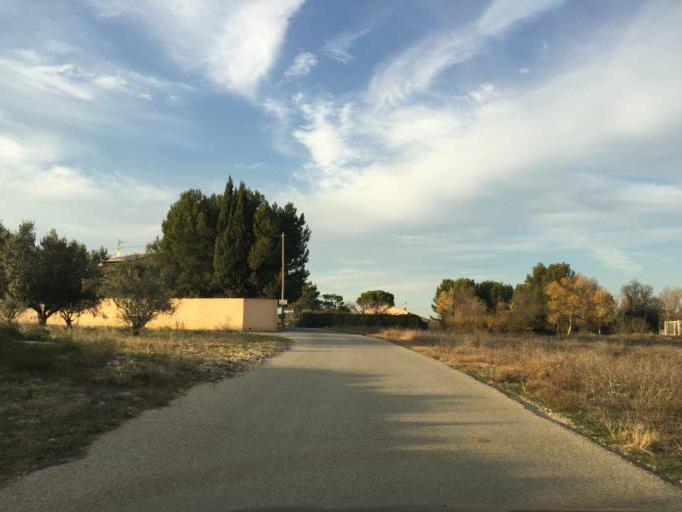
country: FR
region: Provence-Alpes-Cote d'Azur
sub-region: Departement du Vaucluse
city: Bedarrides
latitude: 44.0576
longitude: 4.8914
